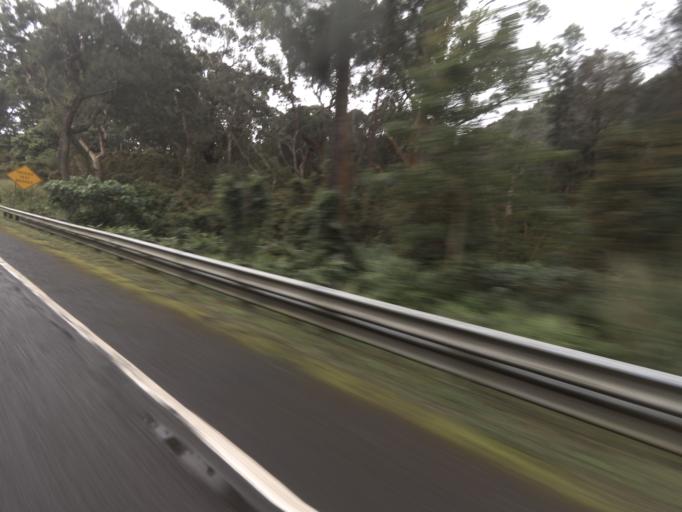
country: US
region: Hawaii
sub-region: Honolulu County
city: Kane'ohe
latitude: 21.3743
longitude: -157.8224
